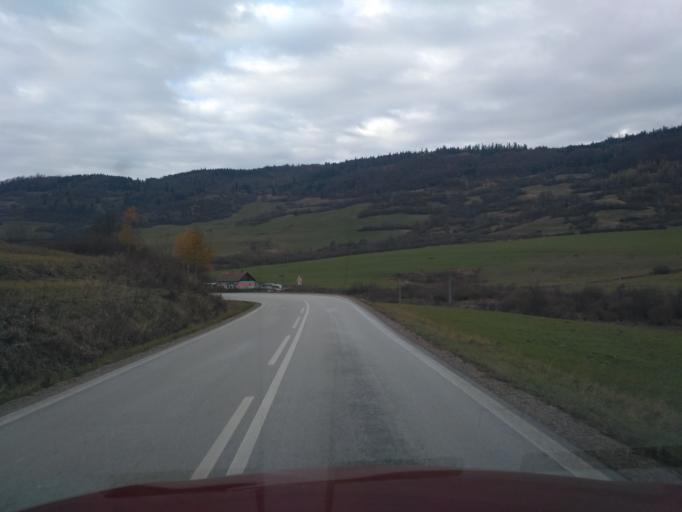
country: SK
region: Kosicky
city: Spisska Nova Ves
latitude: 48.8357
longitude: 20.6458
